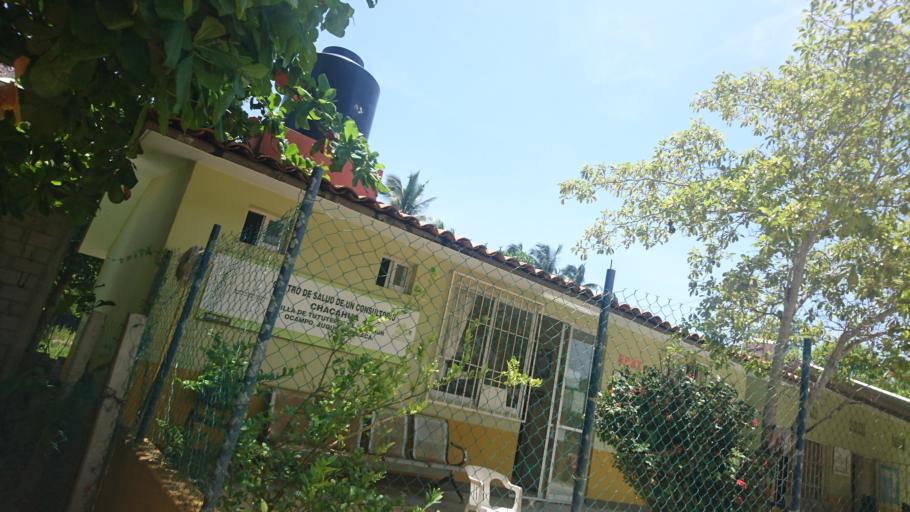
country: MX
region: Oaxaca
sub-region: Villa de Tututepec de Melchor Ocampo
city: Santa Rosa de Lima
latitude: 15.9701
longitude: -97.6800
